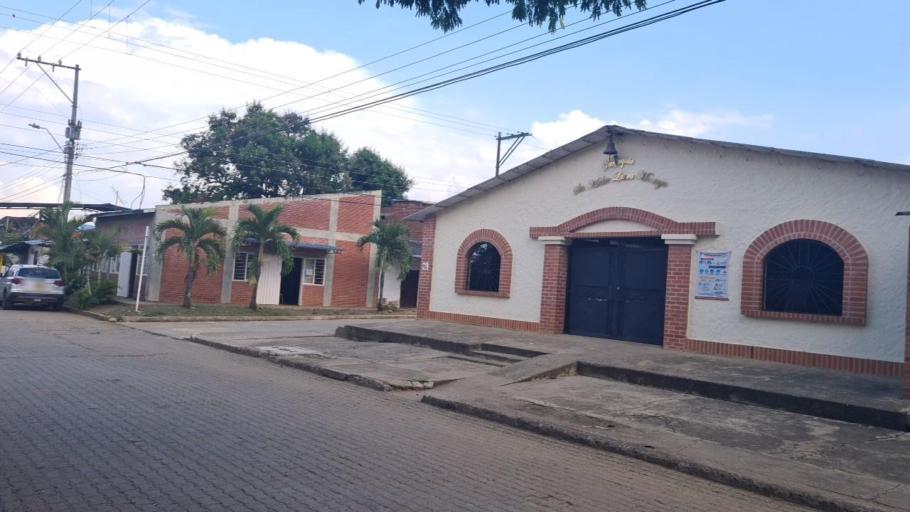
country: CO
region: Valle del Cauca
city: Jamundi
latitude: 3.2282
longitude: -76.5824
